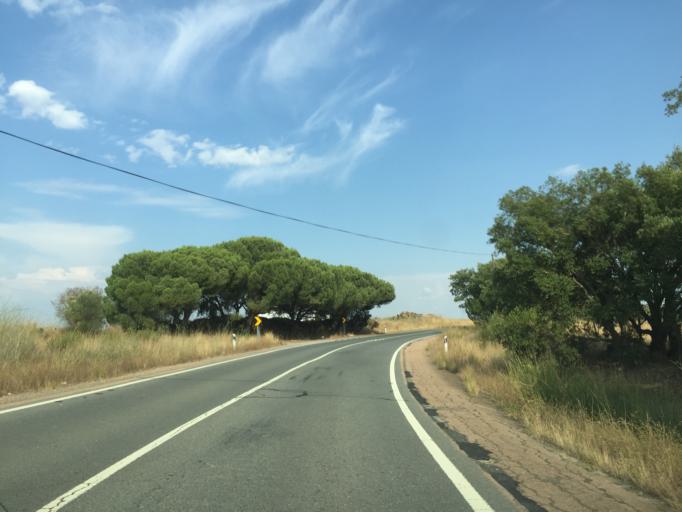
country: PT
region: Beja
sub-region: Aljustrel
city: Aljustrel
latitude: 37.9345
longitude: -8.3560
